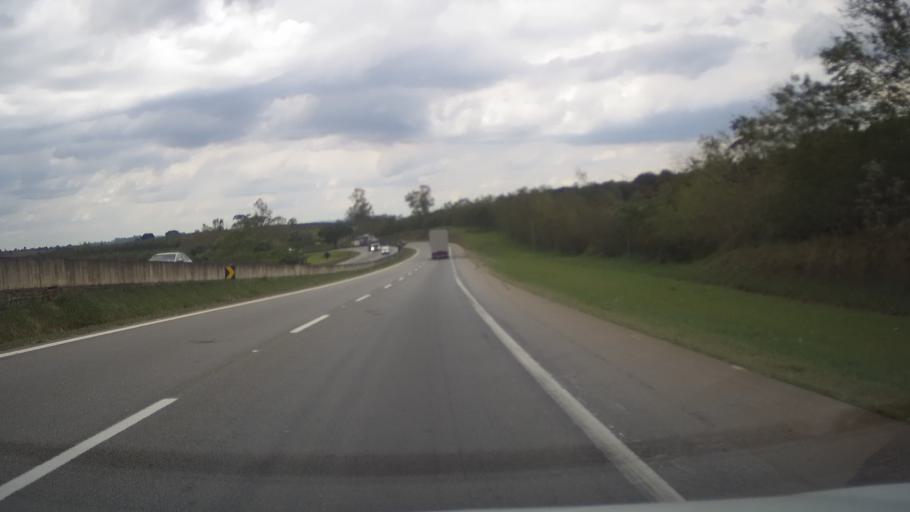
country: BR
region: Minas Gerais
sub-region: Nepomuceno
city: Nepomuceno
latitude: -21.4652
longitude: -45.2060
